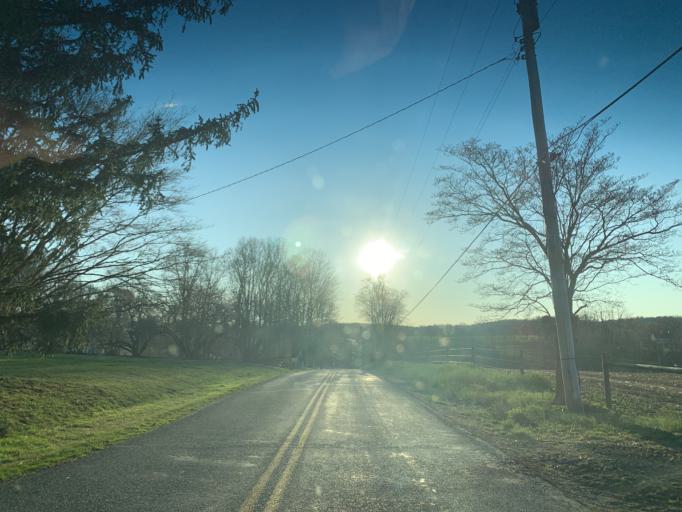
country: US
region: Maryland
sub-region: Harford County
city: South Bel Air
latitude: 39.5955
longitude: -76.2708
